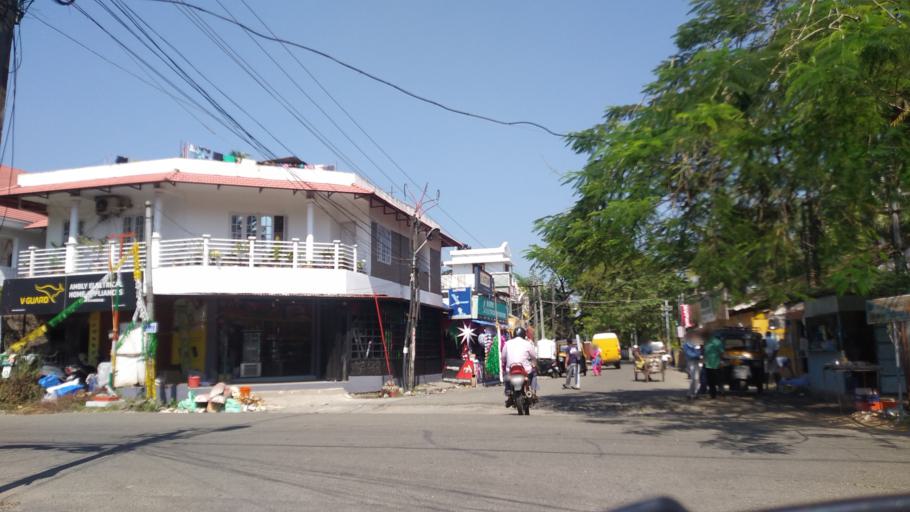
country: IN
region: Kerala
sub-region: Ernakulam
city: Cochin
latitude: 9.9394
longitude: 76.2485
